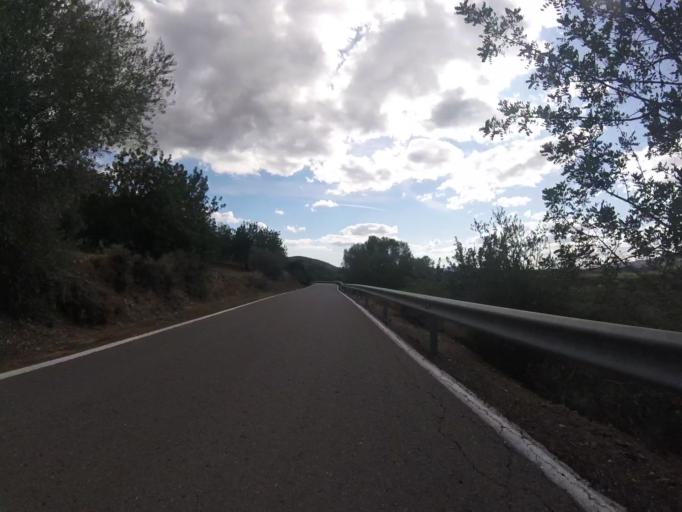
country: ES
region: Valencia
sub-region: Provincia de Castello
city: Cuevas de Vinroma
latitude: 40.3568
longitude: 0.1259
